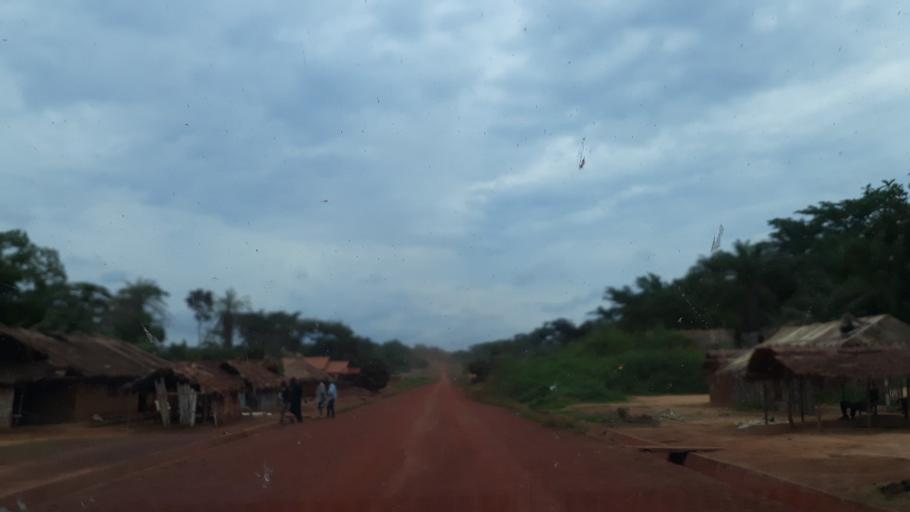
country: CD
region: Eastern Province
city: Kisangani
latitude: 0.6247
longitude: 26.0374
